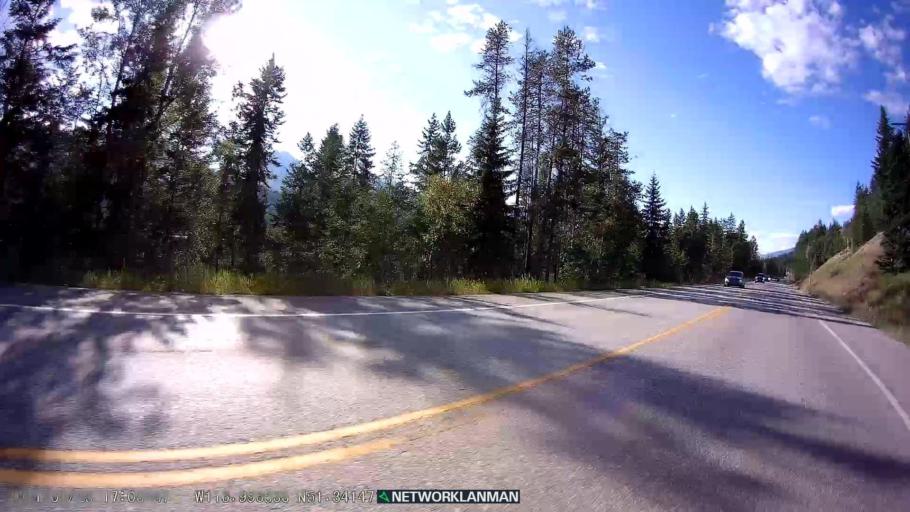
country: CA
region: British Columbia
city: Golden
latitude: 51.3414
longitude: -116.9965
